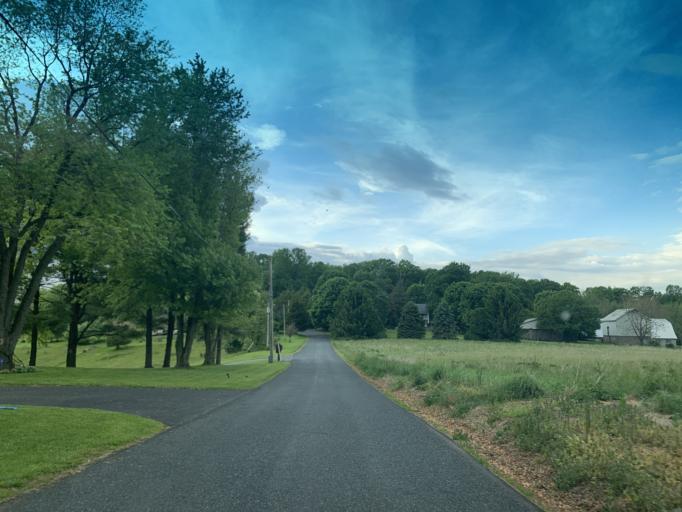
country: US
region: Pennsylvania
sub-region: York County
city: Susquehanna Trails
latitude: 39.6737
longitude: -76.2679
